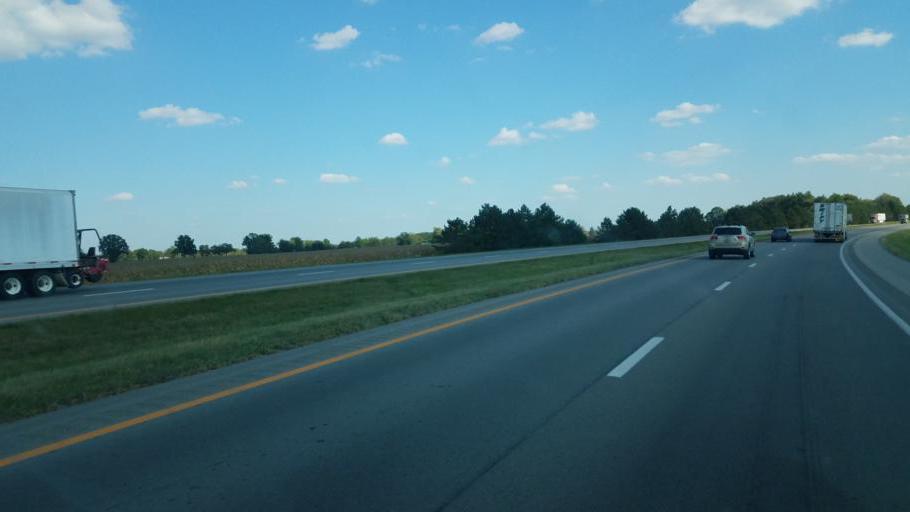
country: US
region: Ohio
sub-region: Wyandot County
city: Upper Sandusky
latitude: 40.8572
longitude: -83.2703
